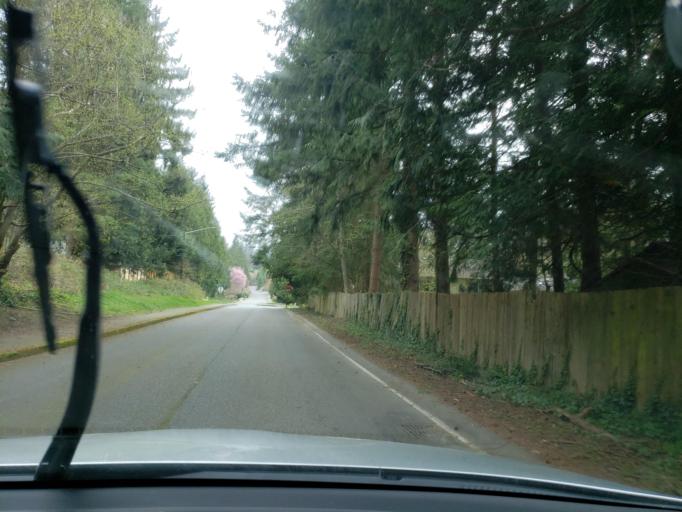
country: US
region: Washington
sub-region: Snohomish County
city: Edmonds
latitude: 47.8153
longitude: -122.3521
